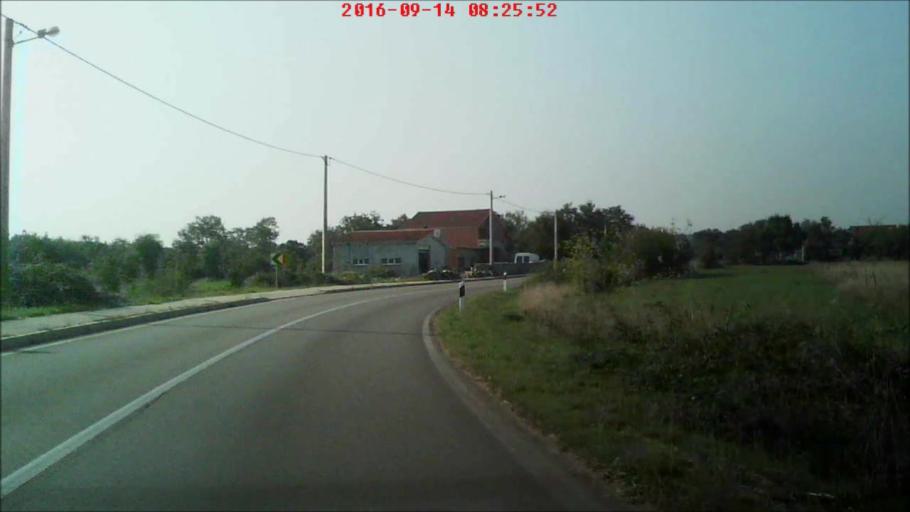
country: HR
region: Zadarska
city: Vrsi
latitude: 44.2004
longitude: 15.2573
